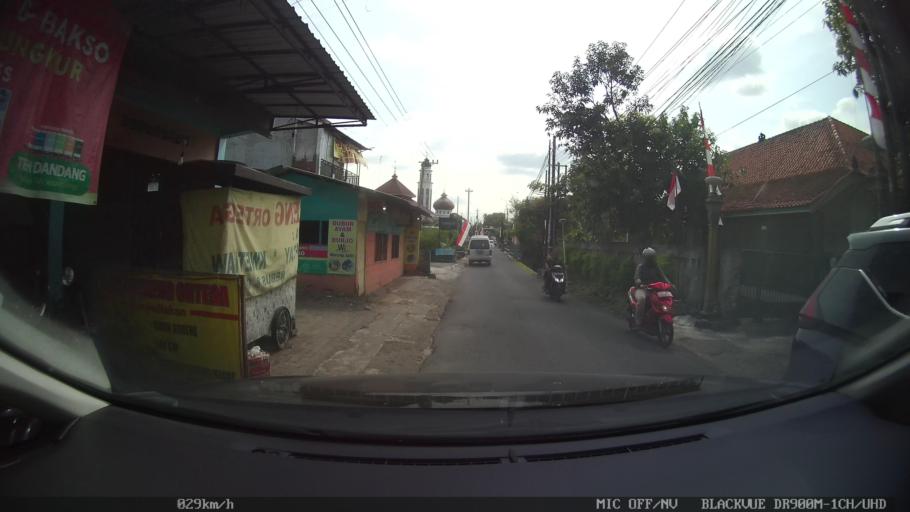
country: ID
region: Daerah Istimewa Yogyakarta
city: Depok
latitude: -7.7611
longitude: 110.4311
